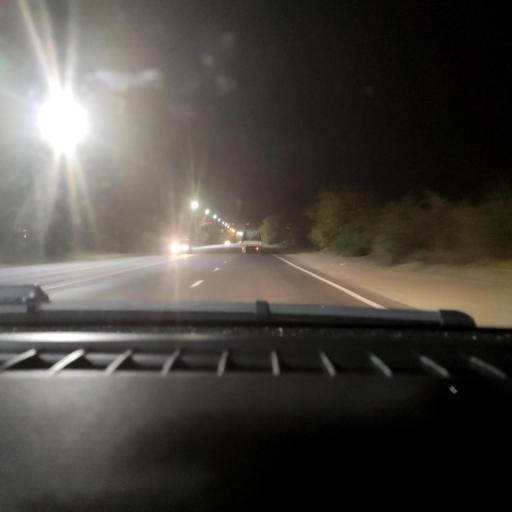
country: RU
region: Voronezj
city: Maslovka
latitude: 51.6222
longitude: 39.2771
